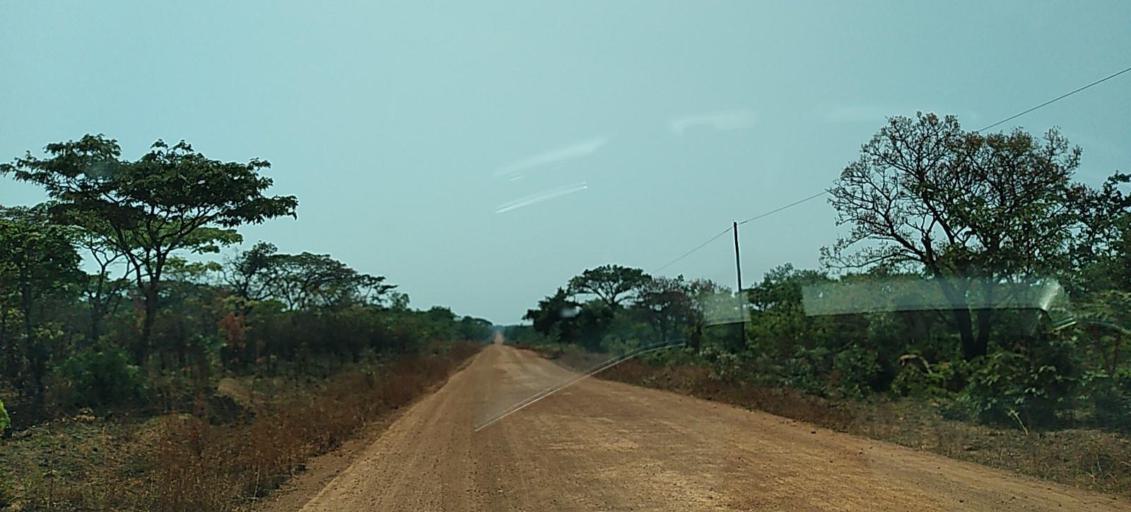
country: ZM
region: North-Western
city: Kansanshi
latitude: -11.9927
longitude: 26.6240
